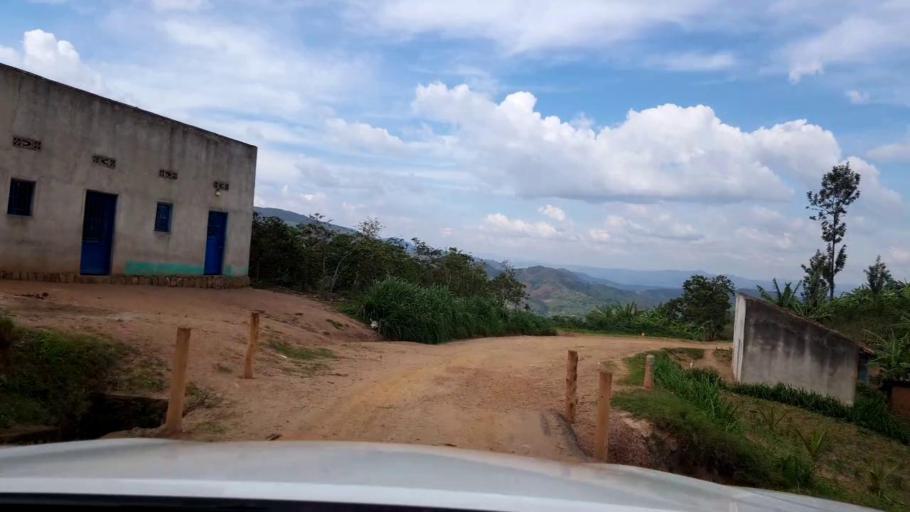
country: RW
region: Southern Province
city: Gitarama
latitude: -1.9835
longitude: 29.7104
